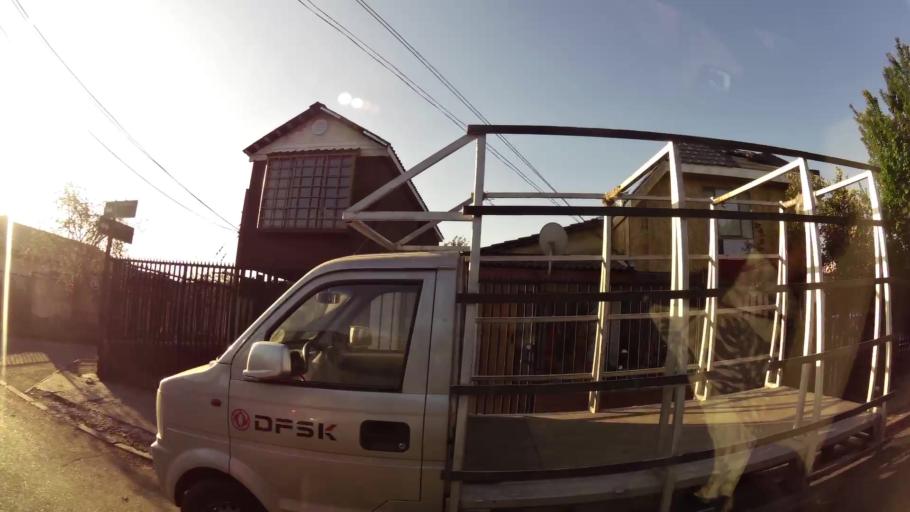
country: CL
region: Santiago Metropolitan
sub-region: Provincia de Santiago
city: La Pintana
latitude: -33.5546
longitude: -70.6199
